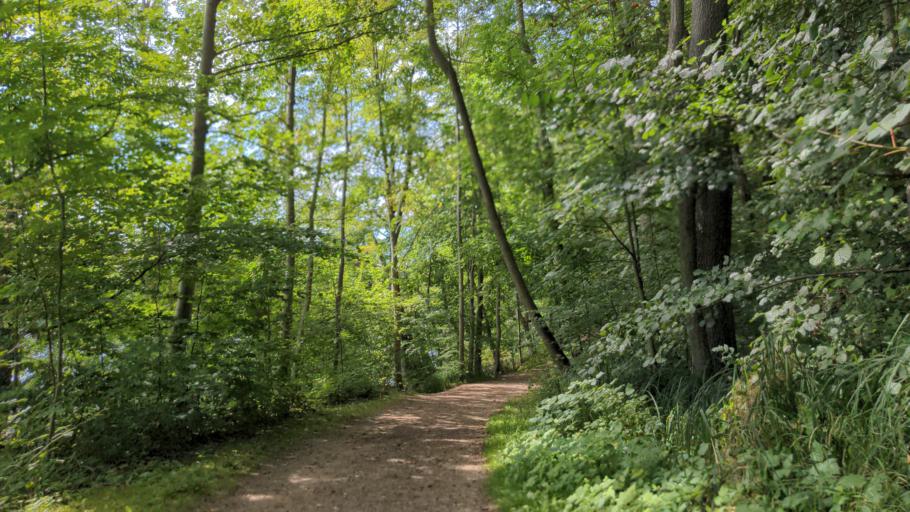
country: DE
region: Schleswig-Holstein
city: Eutin
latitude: 54.1849
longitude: 10.6336
